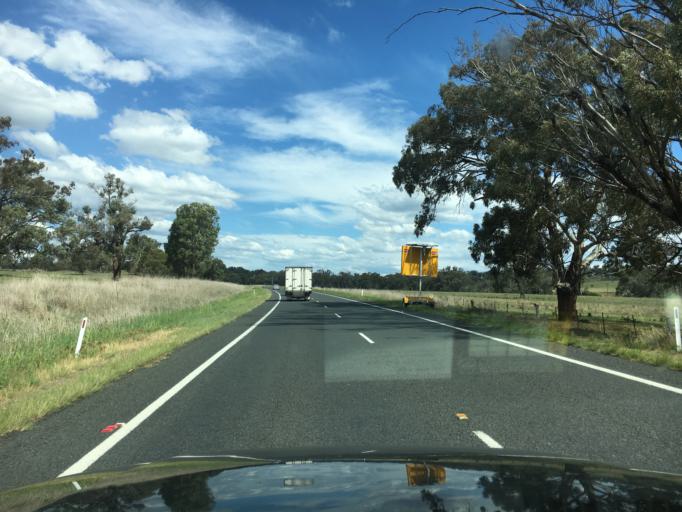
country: AU
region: New South Wales
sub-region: Liverpool Plains
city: Quirindi
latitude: -31.4776
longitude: 150.8611
